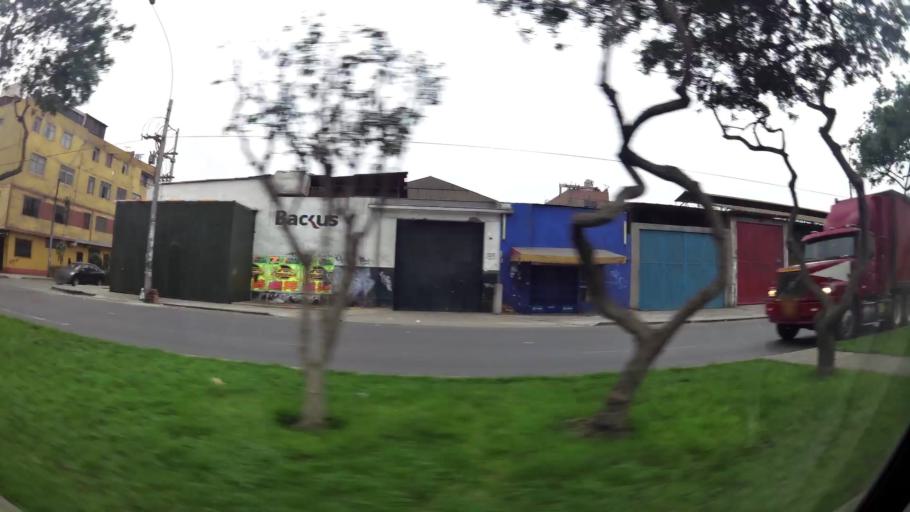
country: PE
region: Lima
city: Lima
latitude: -12.0499
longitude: -77.0599
